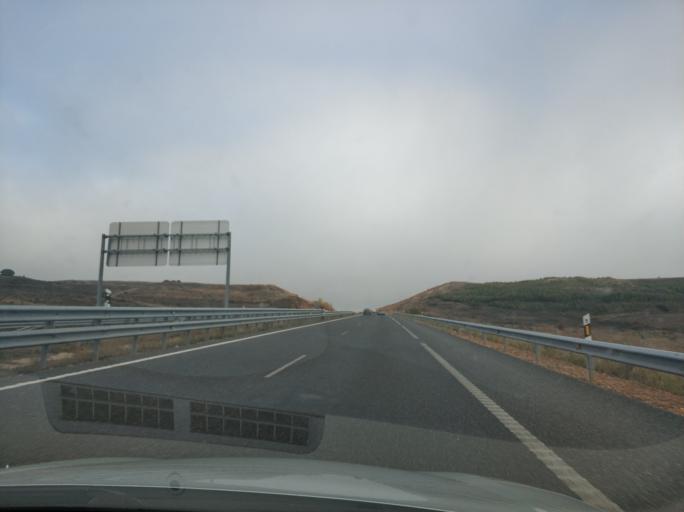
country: ES
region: Castille and Leon
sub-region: Provincia de Leon
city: Leon
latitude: 42.5639
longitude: -5.5356
